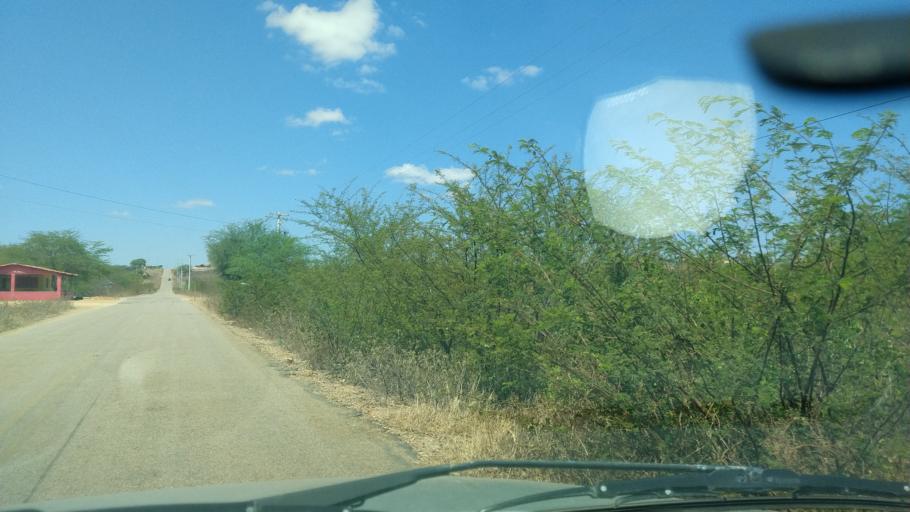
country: BR
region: Rio Grande do Norte
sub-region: Sao Tome
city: Sao Tome
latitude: -5.9660
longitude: -35.9624
